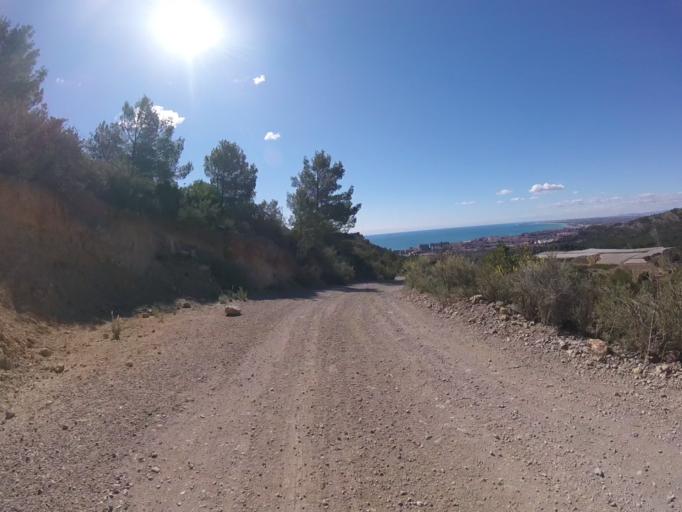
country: ES
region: Valencia
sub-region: Provincia de Castello
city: Benicassim
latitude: 40.0751
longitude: 0.0766
